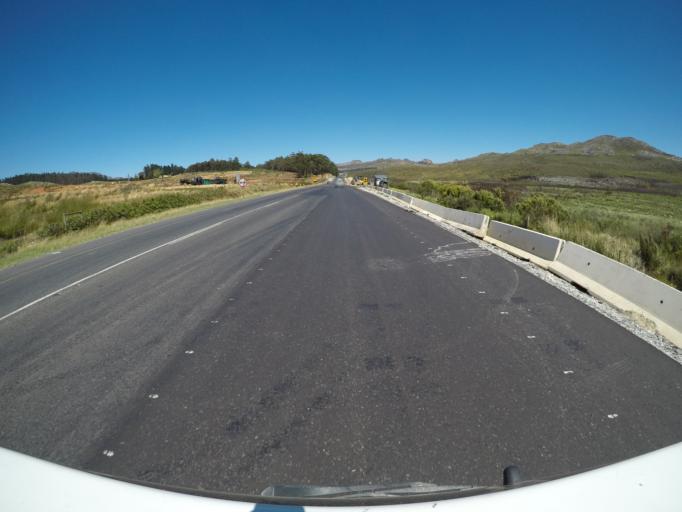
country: ZA
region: Western Cape
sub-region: Overberg District Municipality
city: Grabouw
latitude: -34.1518
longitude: 18.9509
